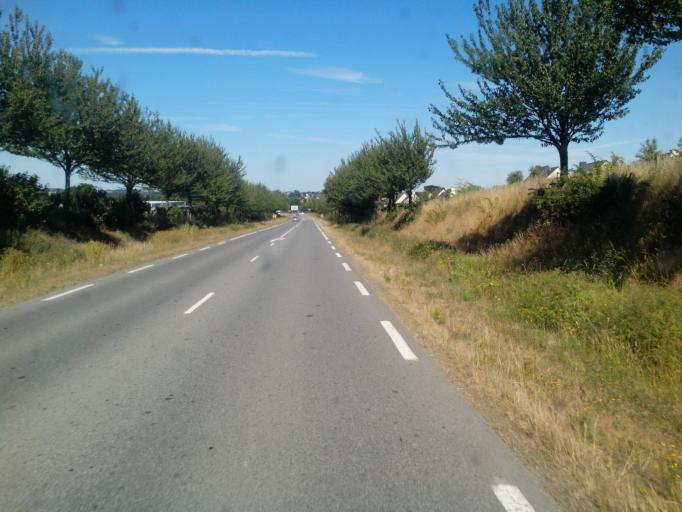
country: FR
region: Brittany
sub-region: Departement d'Ille-et-Vilaine
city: Bain-de-Bretagne
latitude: 47.8517
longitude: -1.6864
